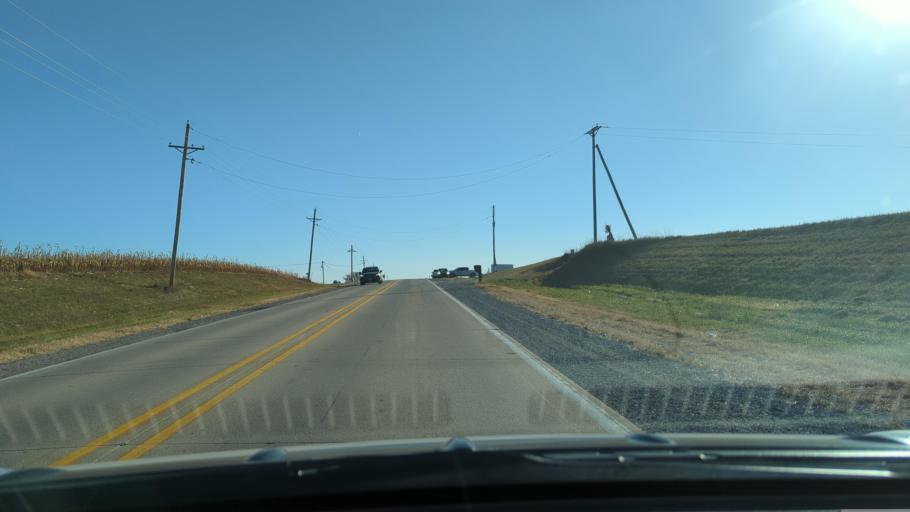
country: US
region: Nebraska
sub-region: Sarpy County
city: Papillion
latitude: 41.0925
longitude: -96.0267
